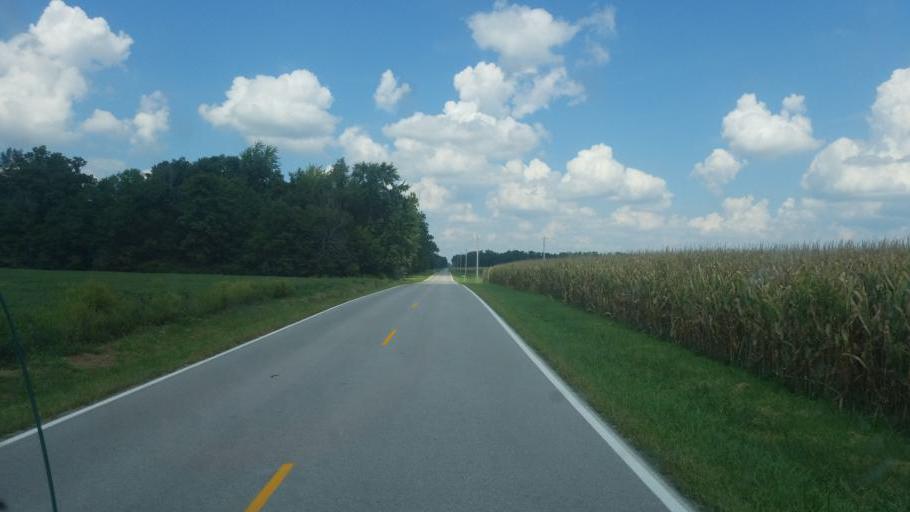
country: US
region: Ohio
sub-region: Hancock County
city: Arlington
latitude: 40.8400
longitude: -83.7277
